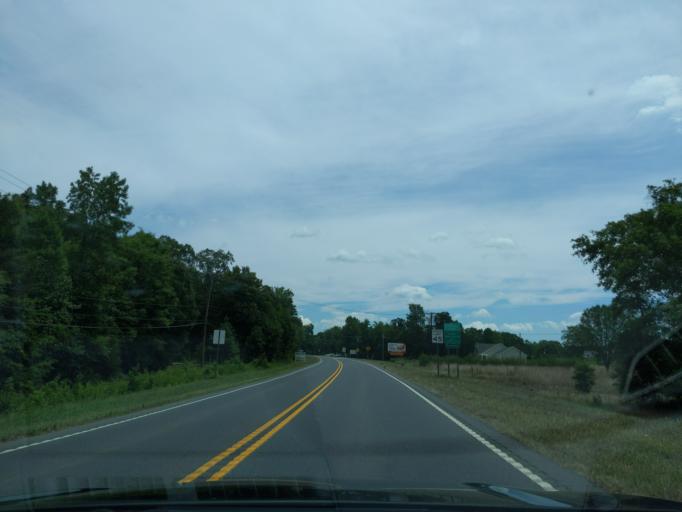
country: US
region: North Carolina
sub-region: Stanly County
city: Albemarle
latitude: 35.4697
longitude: -80.2730
